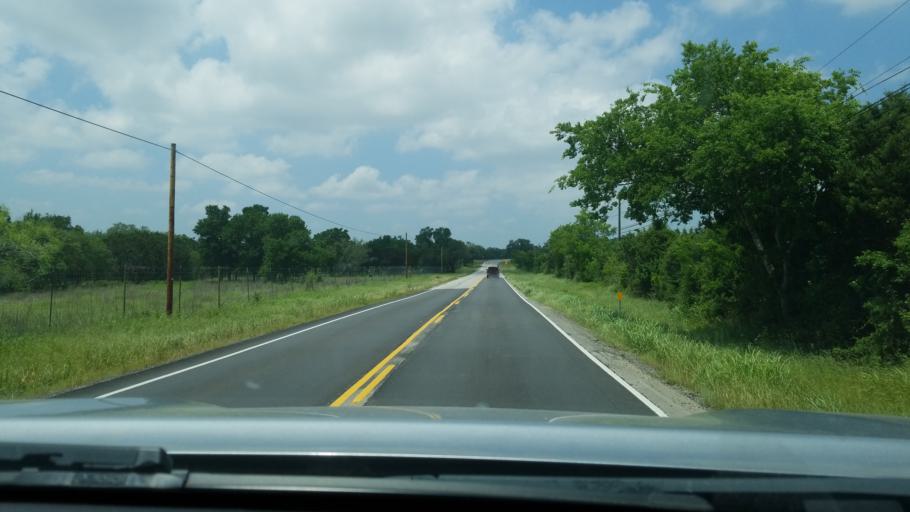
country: US
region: Texas
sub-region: Hays County
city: Dripping Springs
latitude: 30.1517
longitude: -98.0629
